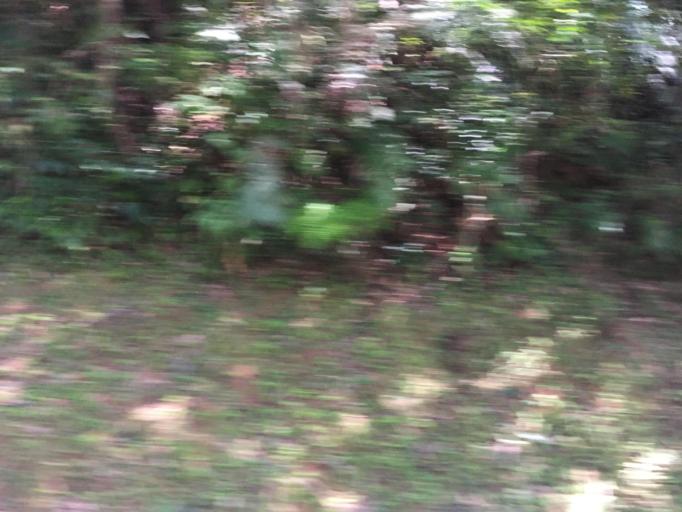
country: TW
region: Taiwan
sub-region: Yilan
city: Yilan
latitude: 24.7557
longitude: 121.6204
